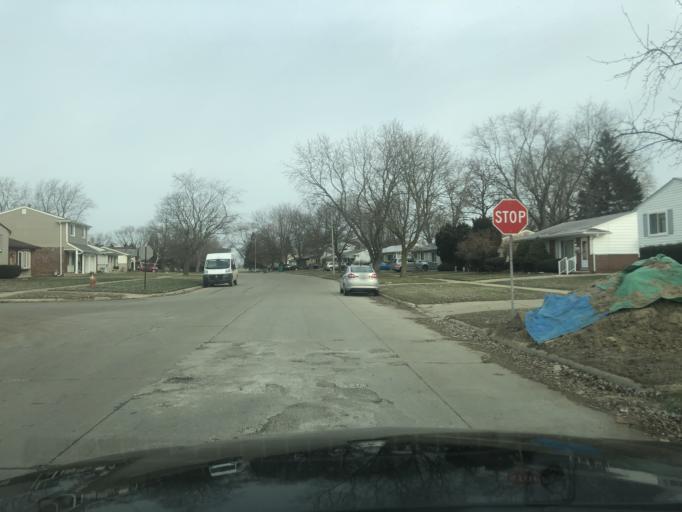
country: US
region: Michigan
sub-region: Wayne County
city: Taylor
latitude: 42.1929
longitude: -83.3158
